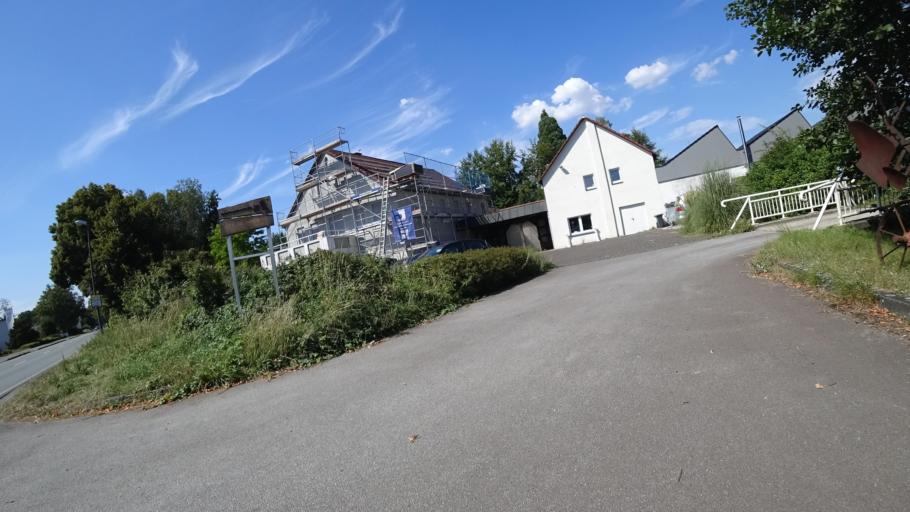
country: DE
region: North Rhine-Westphalia
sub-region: Regierungsbezirk Detmold
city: Guetersloh
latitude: 51.9450
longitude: 8.4234
